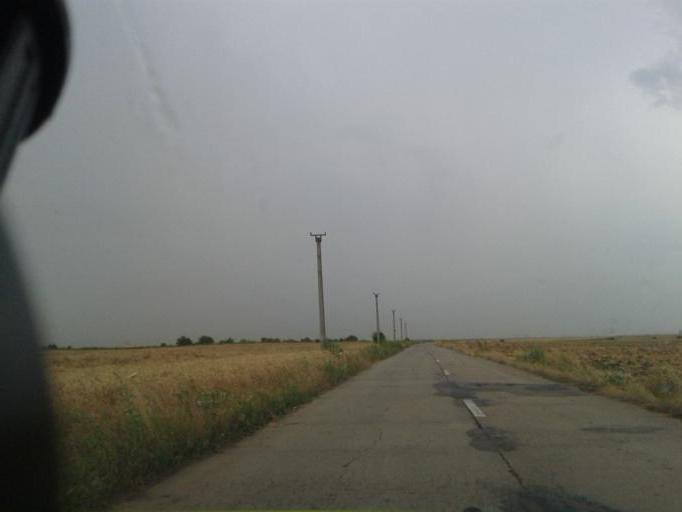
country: RO
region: Ialomita
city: Sinesti
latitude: 44.5404
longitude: 26.3950
